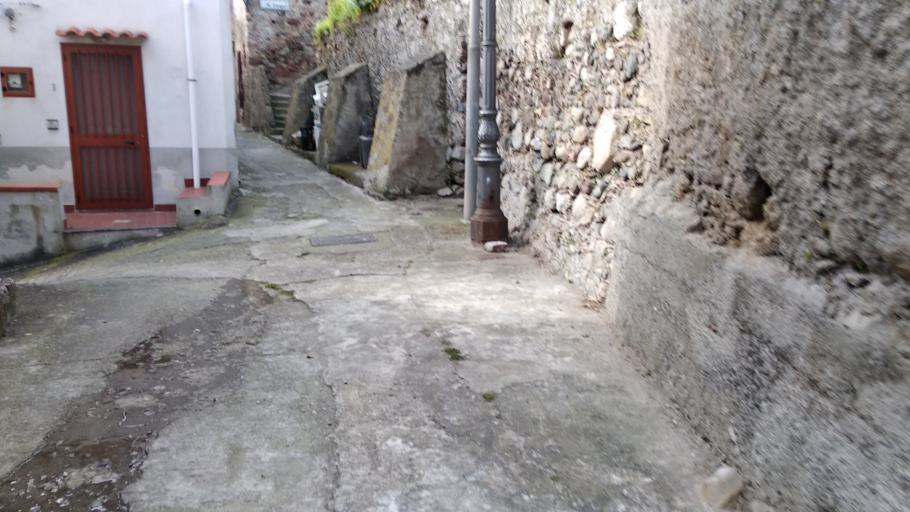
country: IT
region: Sicily
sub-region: Messina
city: Villafranca Tirrena
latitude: 38.2235
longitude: 15.4514
